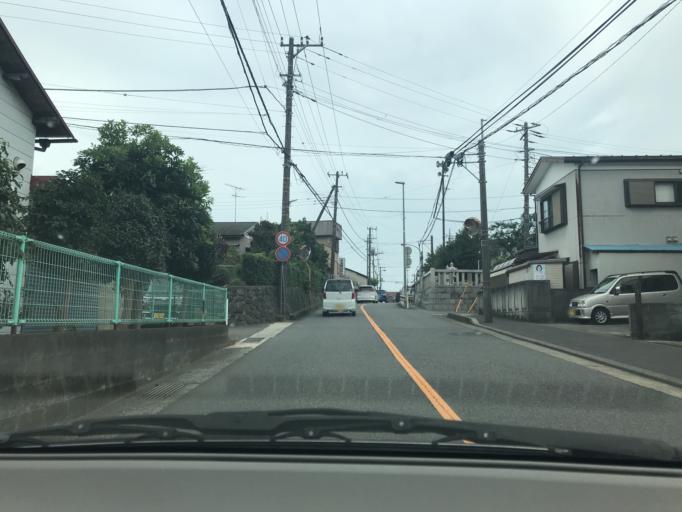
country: JP
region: Kanagawa
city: Fujisawa
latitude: 35.3846
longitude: 139.4388
